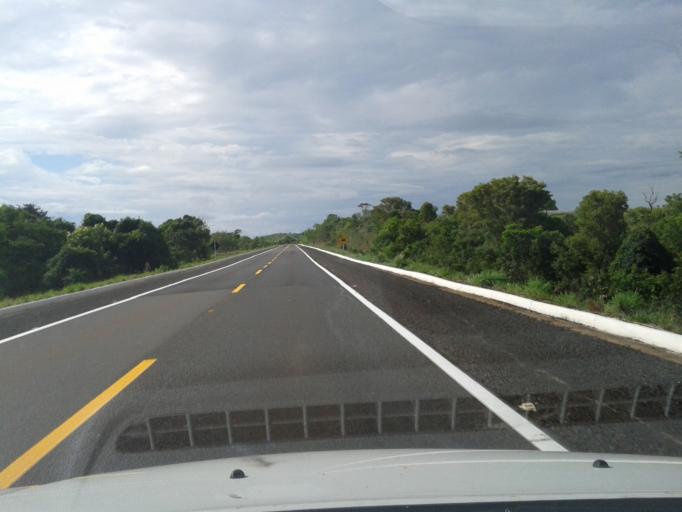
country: BR
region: Minas Gerais
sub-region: Campina Verde
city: Campina Verde
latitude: -19.3097
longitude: -49.6633
